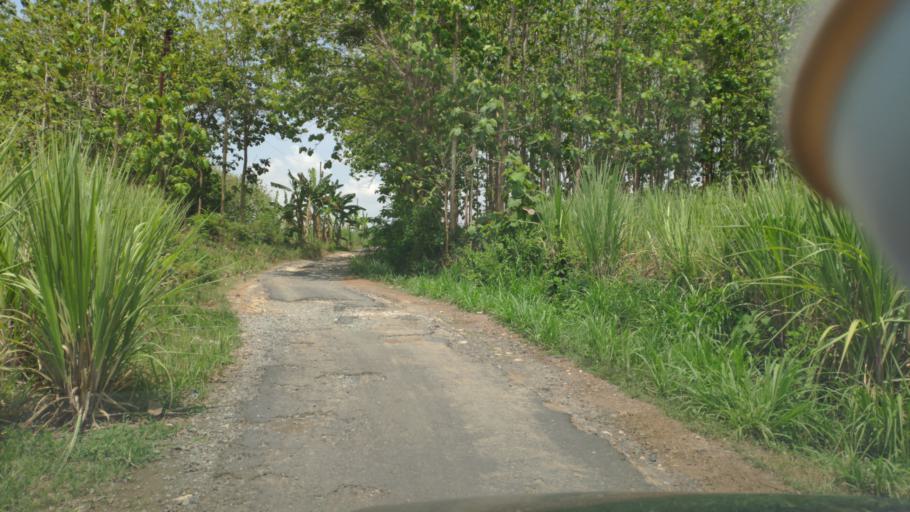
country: ID
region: Central Java
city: Jepang
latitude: -7.0106
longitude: 111.2386
